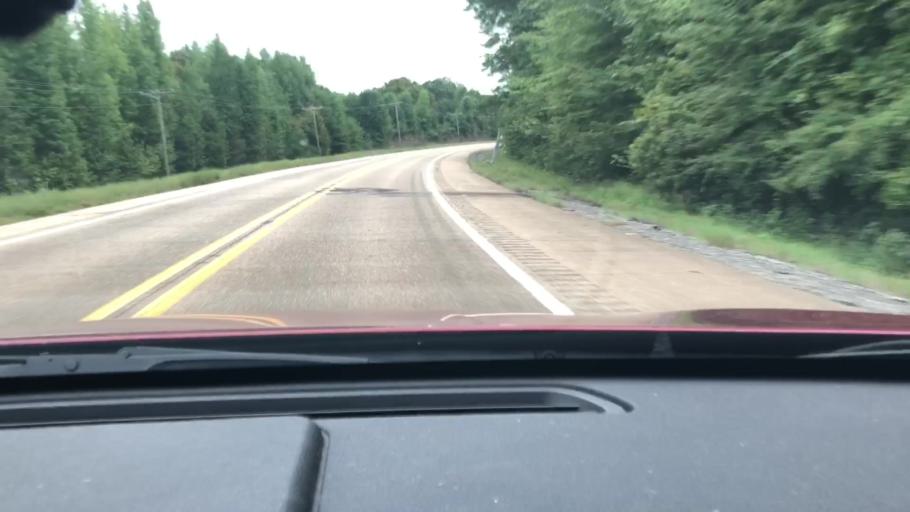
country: US
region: Arkansas
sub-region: Miller County
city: Texarkana
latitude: 33.4188
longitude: -93.8160
